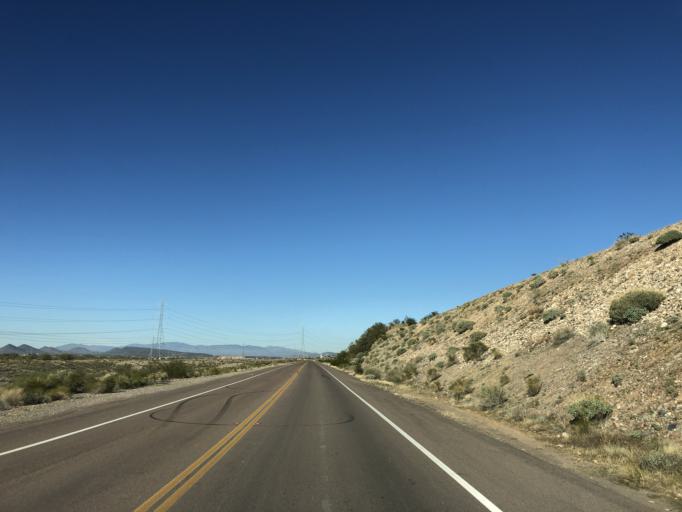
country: US
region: Arizona
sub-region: Maricopa County
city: Sun City West
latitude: 33.6825
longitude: -112.2977
